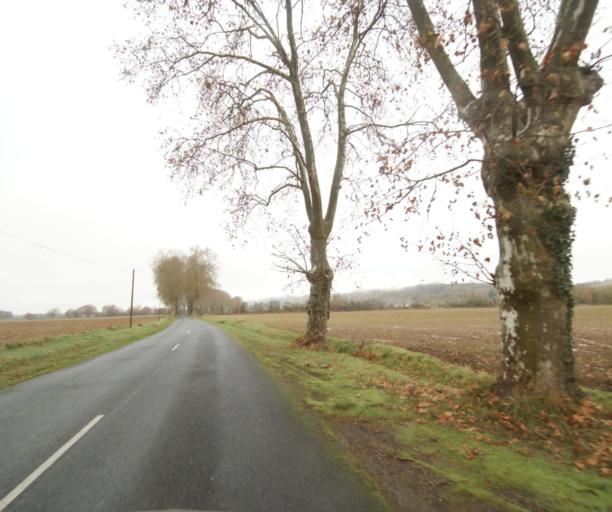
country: FR
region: Midi-Pyrenees
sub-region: Departement de la Haute-Garonne
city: Villemur-sur-Tarn
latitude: 43.8786
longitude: 1.4857
